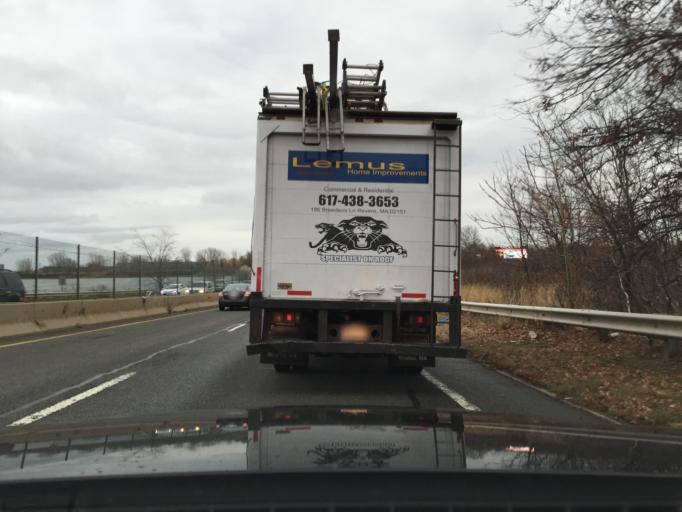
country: US
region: Massachusetts
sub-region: Suffolk County
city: Revere
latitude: 42.4344
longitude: -71.0190
